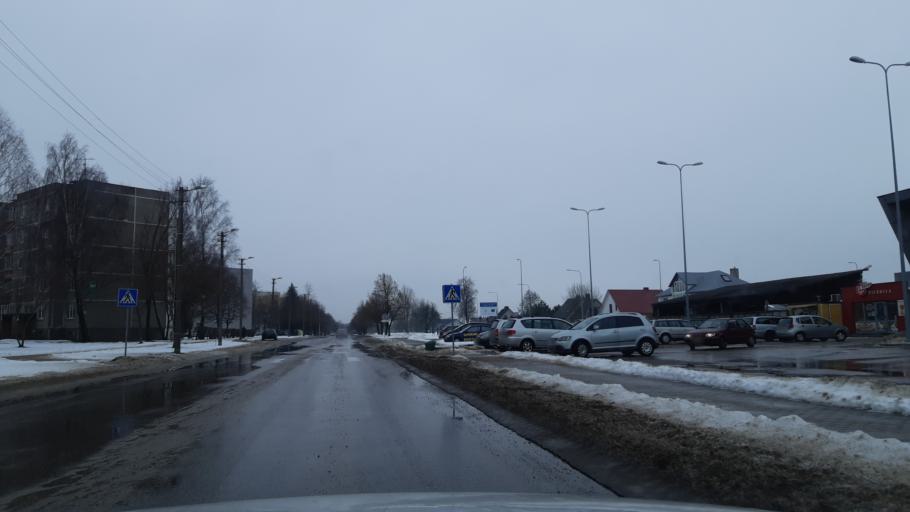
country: LT
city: Vilkaviskis
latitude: 54.6586
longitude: 23.0306
